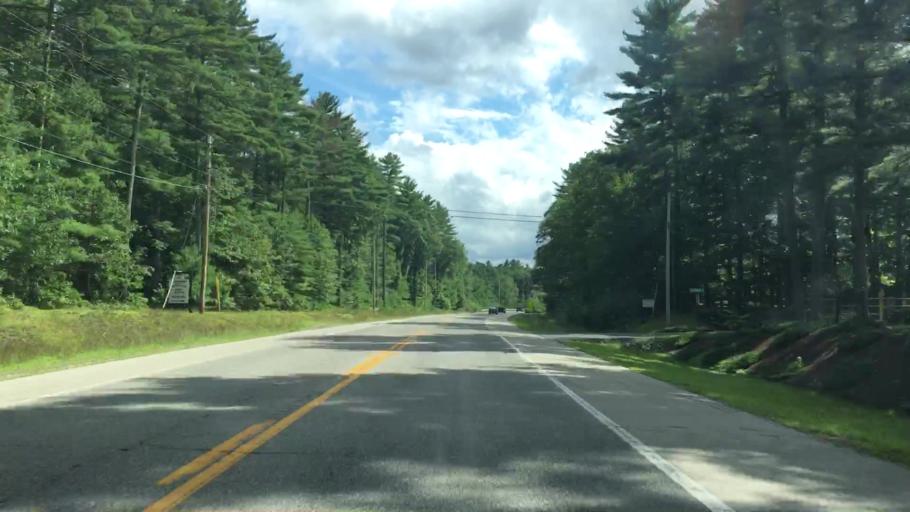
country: US
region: Maine
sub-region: York County
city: South Sanford
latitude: 43.3608
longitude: -70.7292
